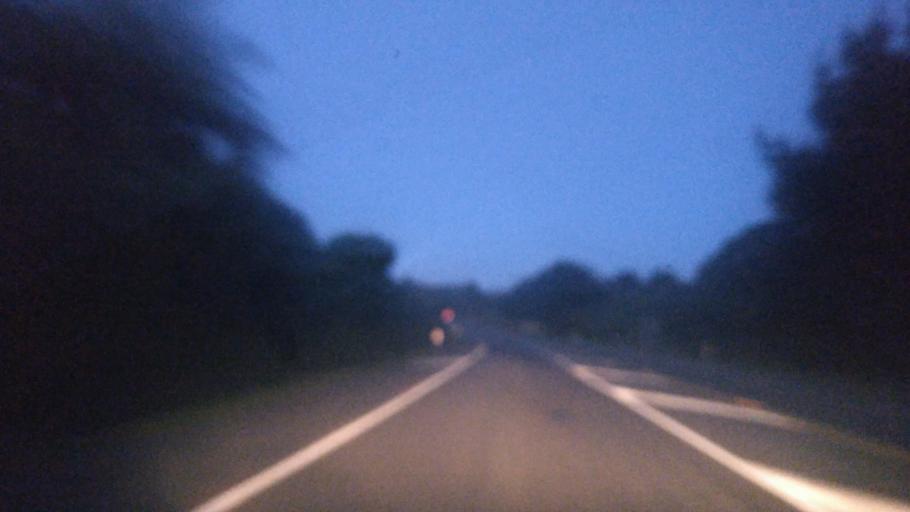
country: NZ
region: Wellington
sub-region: Porirua City
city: Porirua
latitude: -41.0463
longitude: 174.8811
